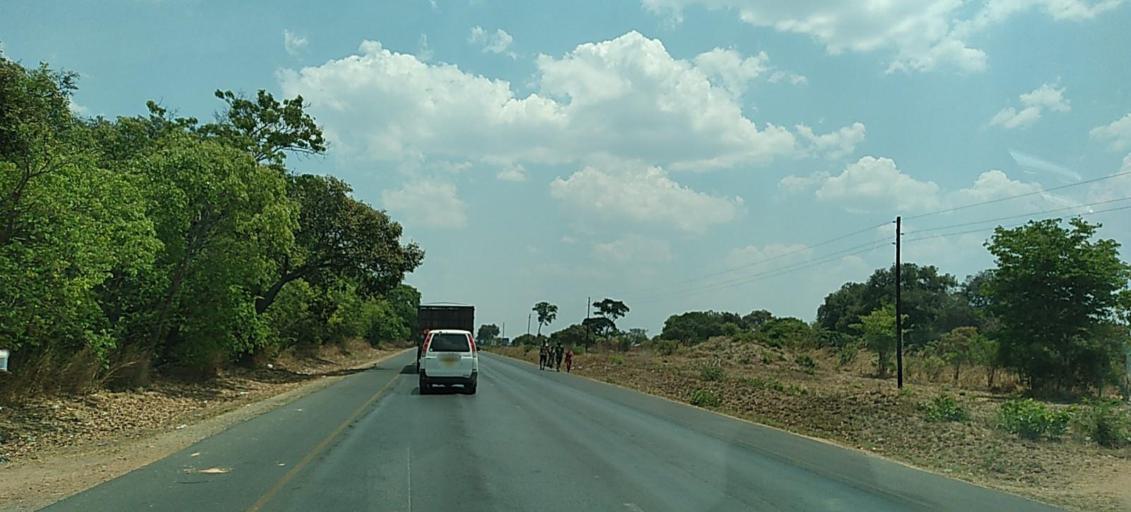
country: ZM
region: Central
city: Kabwe
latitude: -14.2294
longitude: 28.5728
